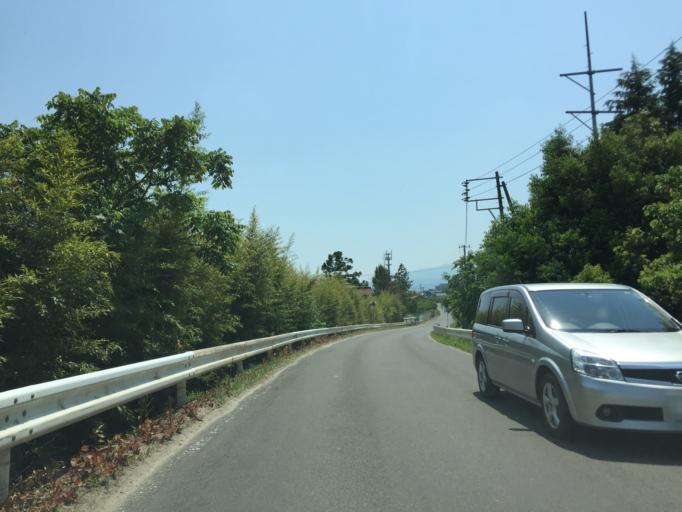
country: JP
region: Fukushima
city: Fukushima-shi
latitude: 37.8142
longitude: 140.4768
